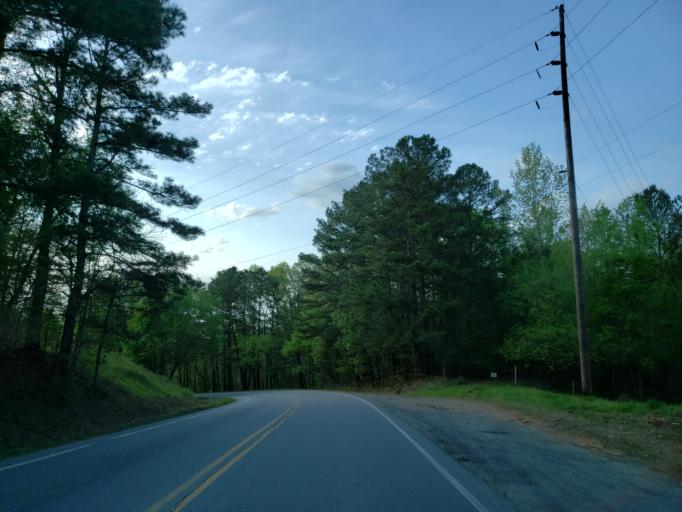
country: US
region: Georgia
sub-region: Cherokee County
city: Ball Ground
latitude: 34.2930
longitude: -84.3910
